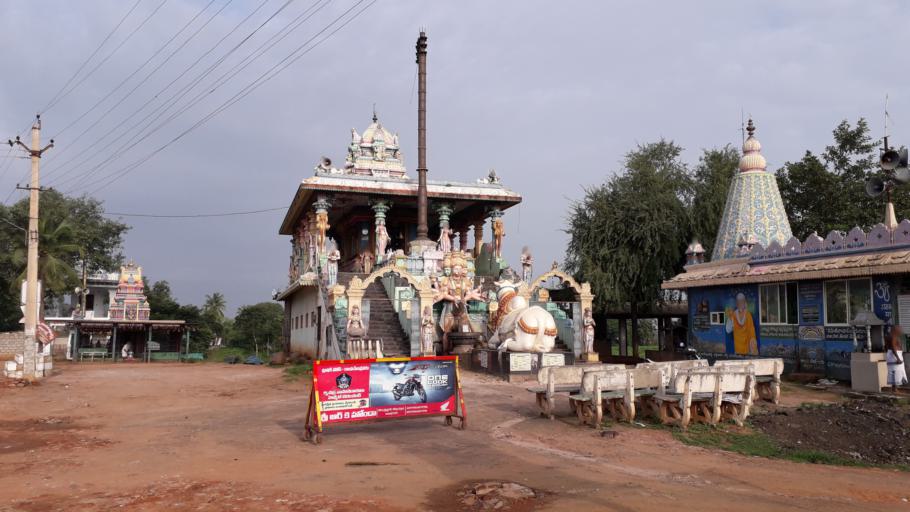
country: IN
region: Andhra Pradesh
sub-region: East Godavari
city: Rajahmundry
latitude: 17.0463
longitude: 81.8436
